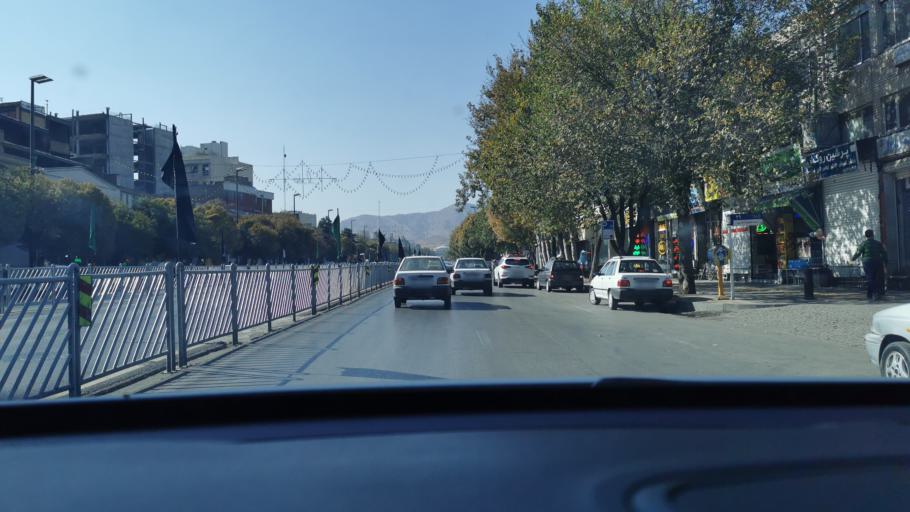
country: IR
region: Razavi Khorasan
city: Mashhad
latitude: 36.2725
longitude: 59.6024
